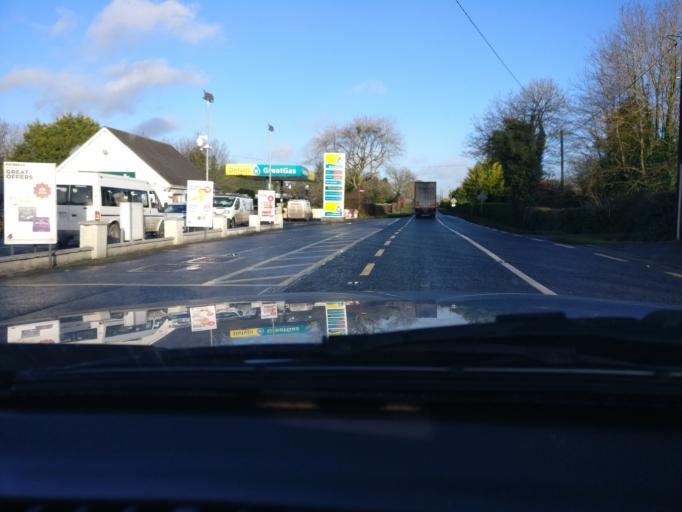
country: IE
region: Leinster
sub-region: An Iarmhi
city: Rathwire
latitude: 53.6231
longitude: -7.0810
